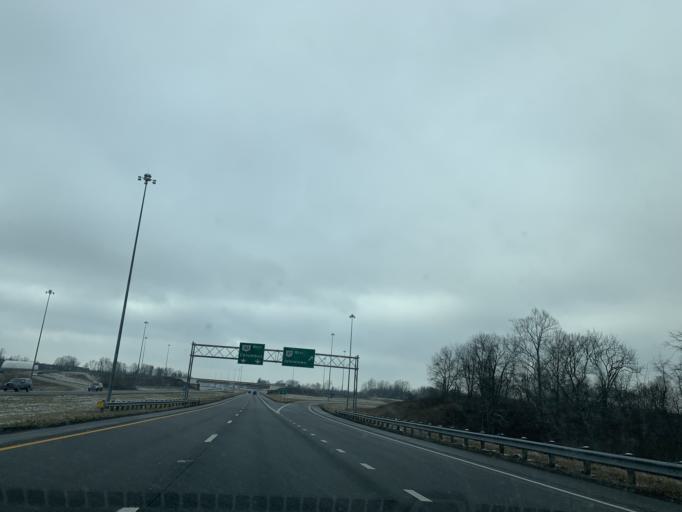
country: US
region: Ohio
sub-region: Licking County
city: Granville South
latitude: 40.0735
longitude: -82.5999
